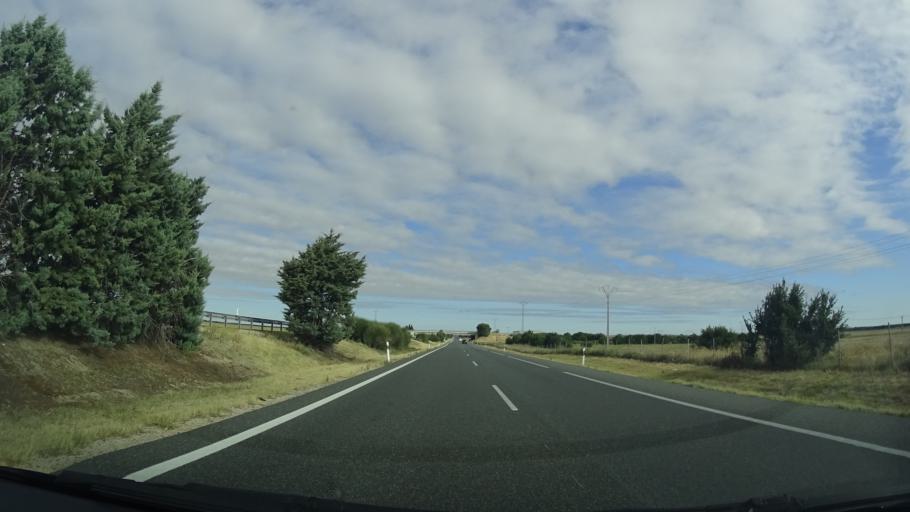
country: ES
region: Castille and Leon
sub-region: Provincia de Valladolid
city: San Vicente del Palacio
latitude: 41.2473
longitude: -4.8683
